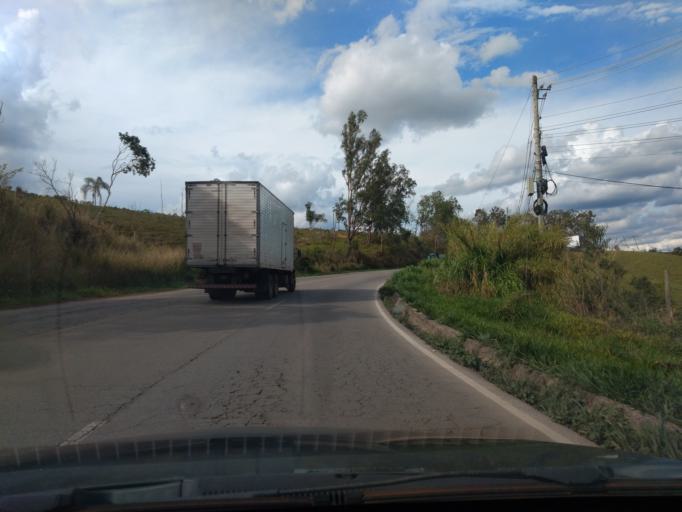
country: BR
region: Minas Gerais
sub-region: Varginha
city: Varginha
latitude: -21.6082
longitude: -45.4330
